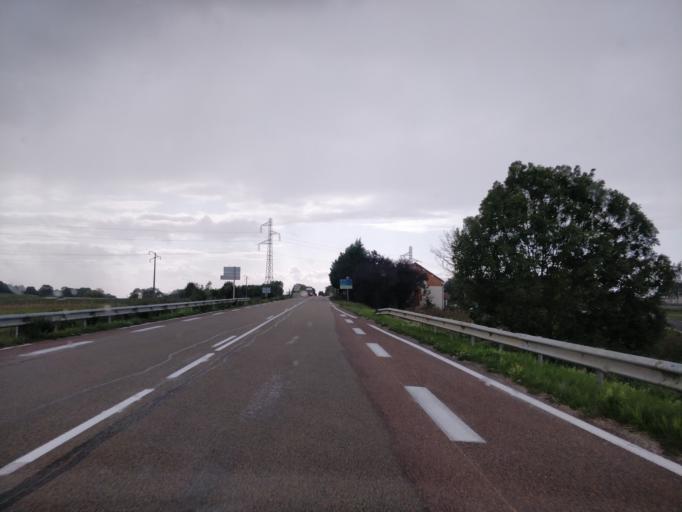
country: FR
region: Champagne-Ardenne
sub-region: Departement de l'Aube
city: Lusigny-sur-Barse
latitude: 48.2409
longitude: 4.3242
